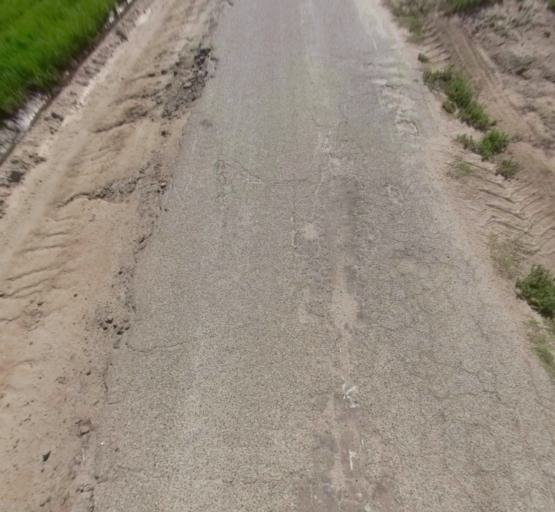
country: US
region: California
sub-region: Madera County
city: Chowchilla
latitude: 37.1273
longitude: -120.3051
